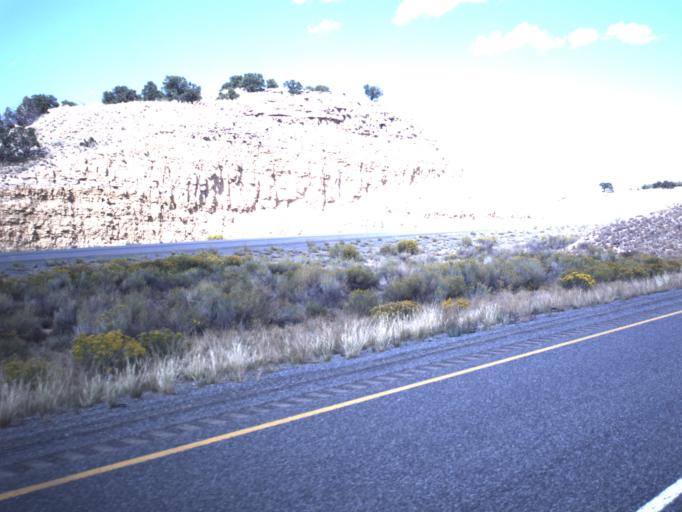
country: US
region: Utah
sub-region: Emery County
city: Castle Dale
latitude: 38.8883
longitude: -110.6476
